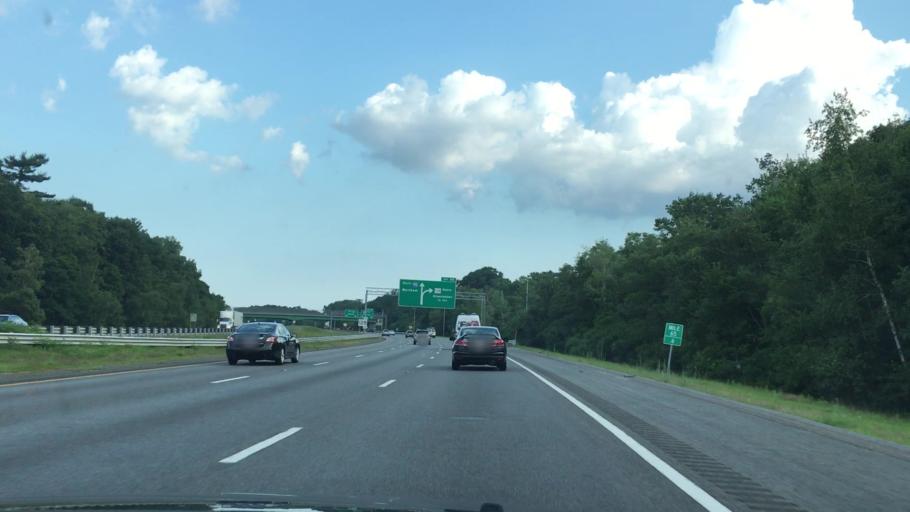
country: US
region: Massachusetts
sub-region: Essex County
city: South Peabody
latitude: 42.5367
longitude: -70.9843
